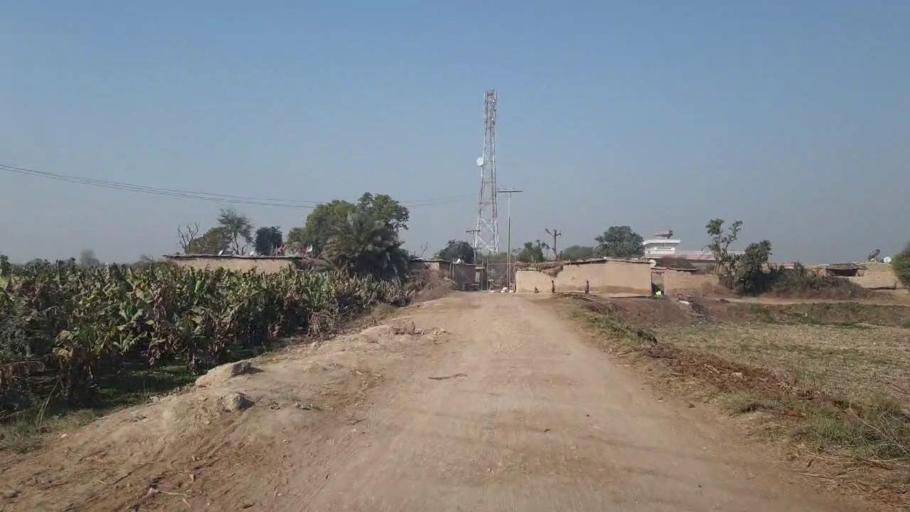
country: PK
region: Sindh
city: Tando Allahyar
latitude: 25.3714
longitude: 68.6656
